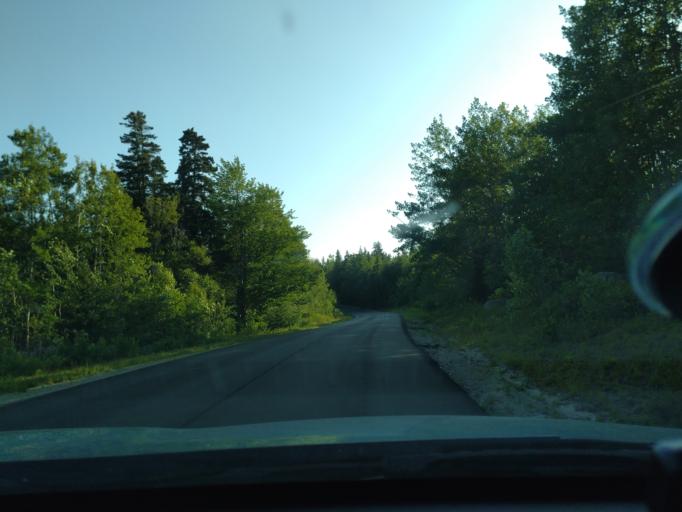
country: US
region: Maine
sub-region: Washington County
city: Eastport
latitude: 44.7113
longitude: -67.1418
